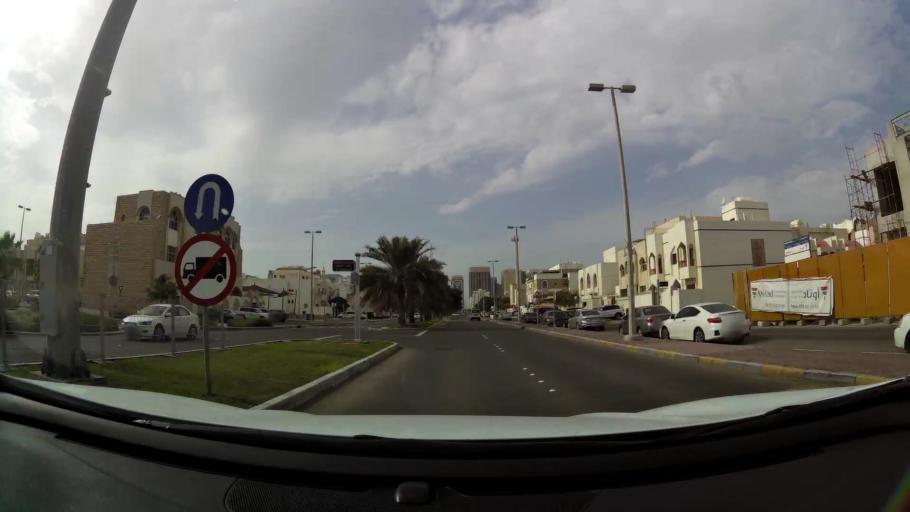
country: AE
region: Abu Dhabi
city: Abu Dhabi
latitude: 24.4653
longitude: 54.3503
